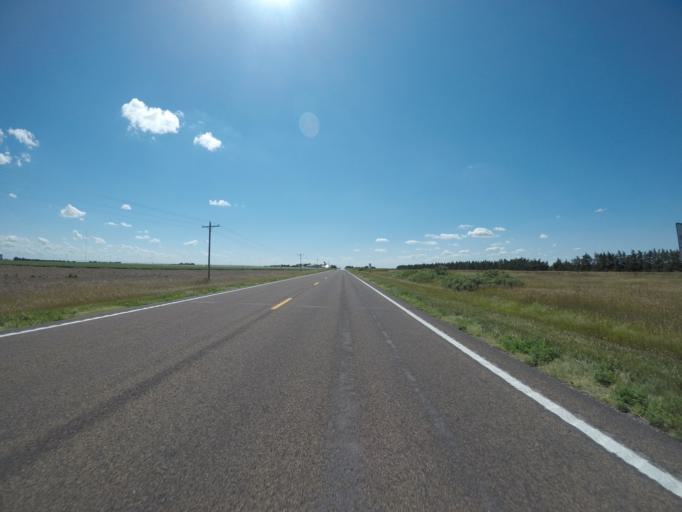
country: US
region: Nebraska
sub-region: Chase County
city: Imperial
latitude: 40.5377
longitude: -101.6579
